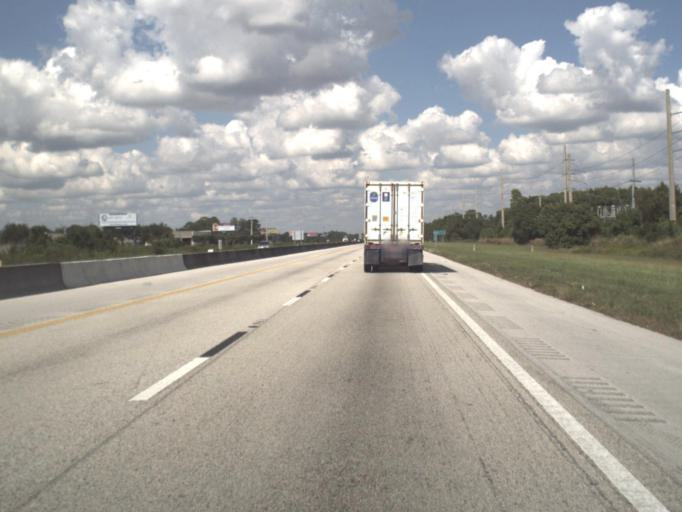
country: US
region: Florida
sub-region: Martin County
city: Palm City
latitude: 27.1655
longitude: -80.3073
